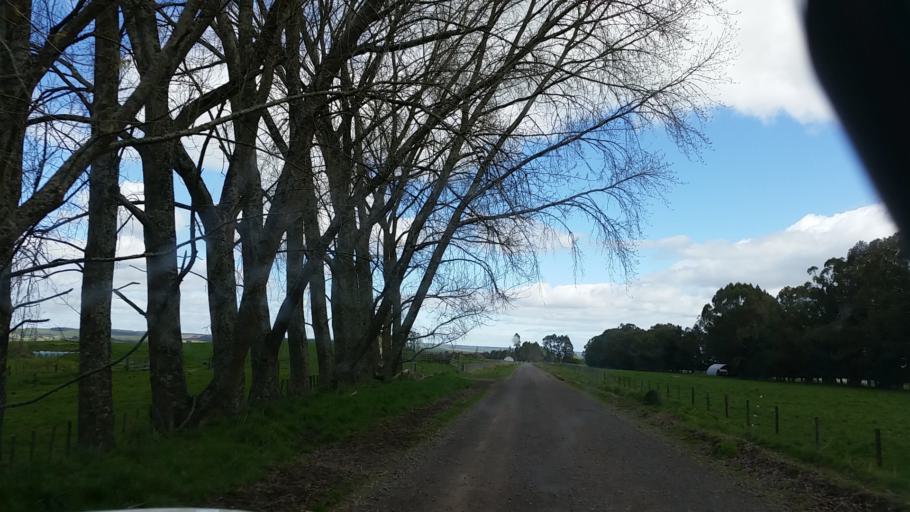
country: NZ
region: Bay of Plenty
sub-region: Whakatane District
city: Murupara
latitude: -38.4719
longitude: 176.4166
